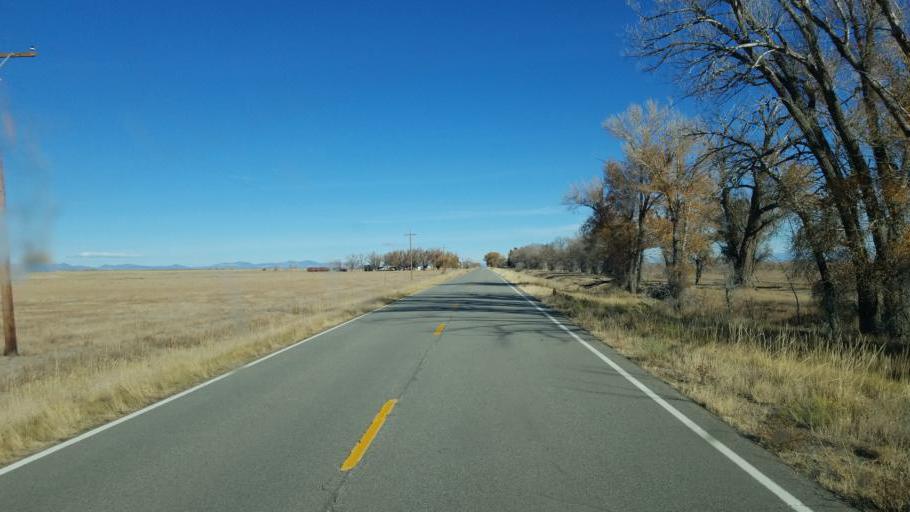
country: US
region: Colorado
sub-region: Rio Grande County
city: Monte Vista
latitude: 37.4794
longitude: -106.1489
